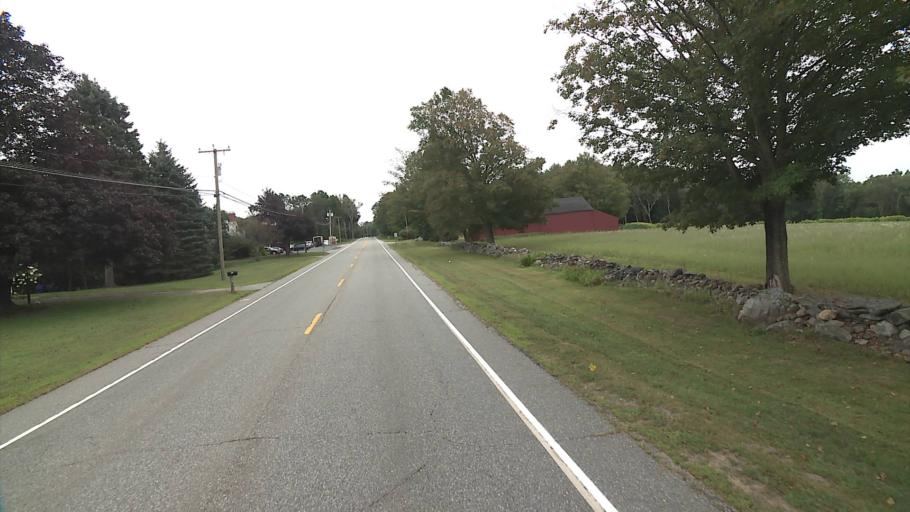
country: US
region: Connecticut
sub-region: Hartford County
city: Manchester
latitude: 41.7514
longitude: -72.4389
